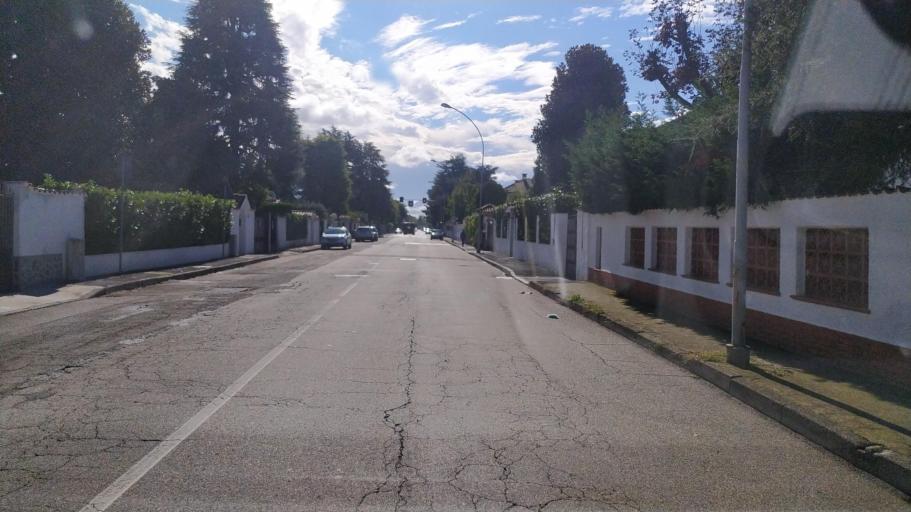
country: IT
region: Lombardy
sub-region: Citta metropolitana di Milano
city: Trezzano sul Naviglio
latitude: 45.4260
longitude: 9.0507
